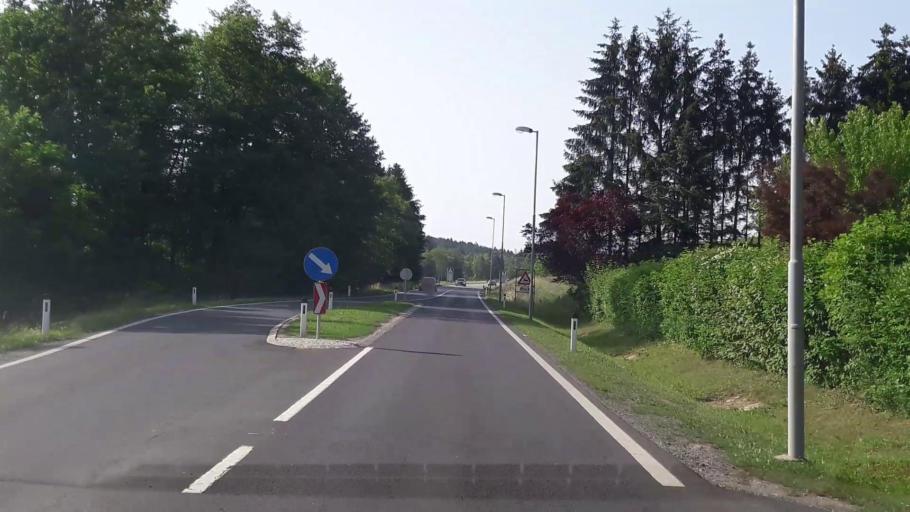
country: AT
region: Burgenland
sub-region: Politischer Bezirk Gussing
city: Ollersdorf im Burgenland
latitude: 47.1905
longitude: 16.1628
